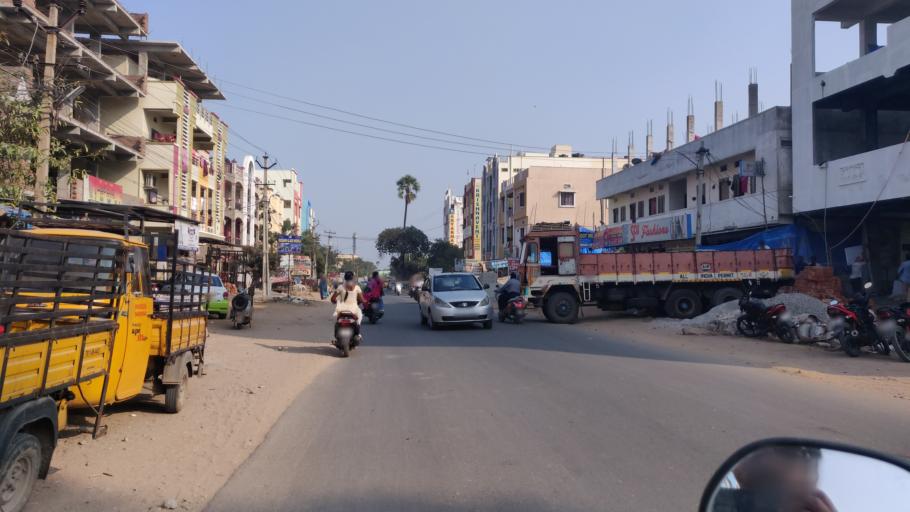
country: IN
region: Telangana
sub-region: Rangareddi
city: Uppal Kalan
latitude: 17.3920
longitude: 78.5979
